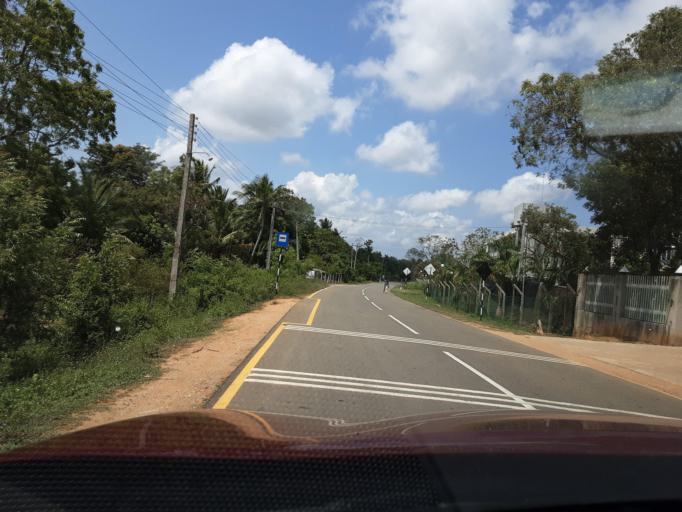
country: LK
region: Southern
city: Tangalla
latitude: 6.2081
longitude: 81.2071
